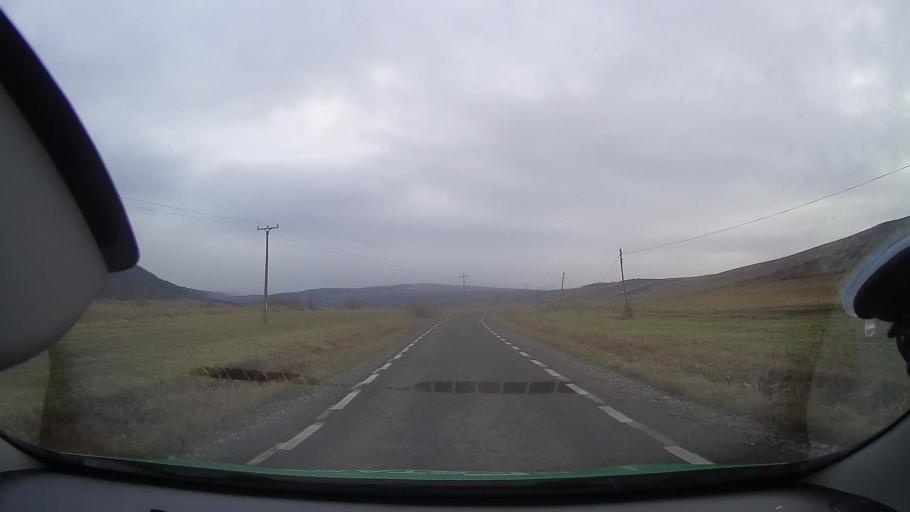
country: RO
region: Mures
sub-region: Comuna Bichis
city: Bichis
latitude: 46.3916
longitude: 24.0890
